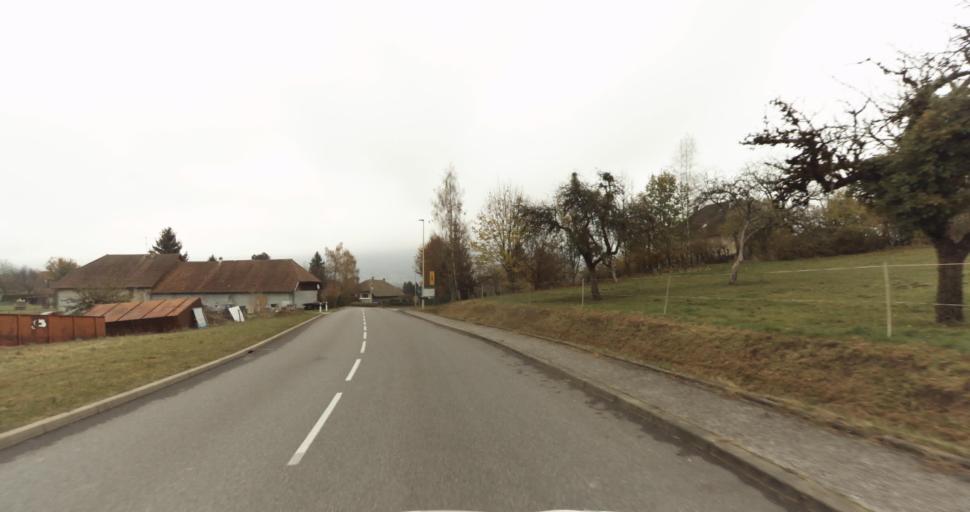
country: FR
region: Rhone-Alpes
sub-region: Departement de la Haute-Savoie
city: Cusy
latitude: 45.7776
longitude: 6.0179
